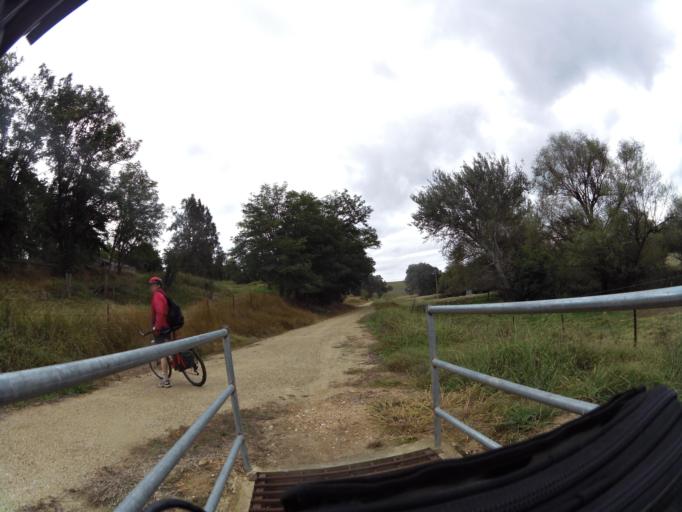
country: AU
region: New South Wales
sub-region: Albury Municipality
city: East Albury
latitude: -36.1946
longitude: 147.3107
